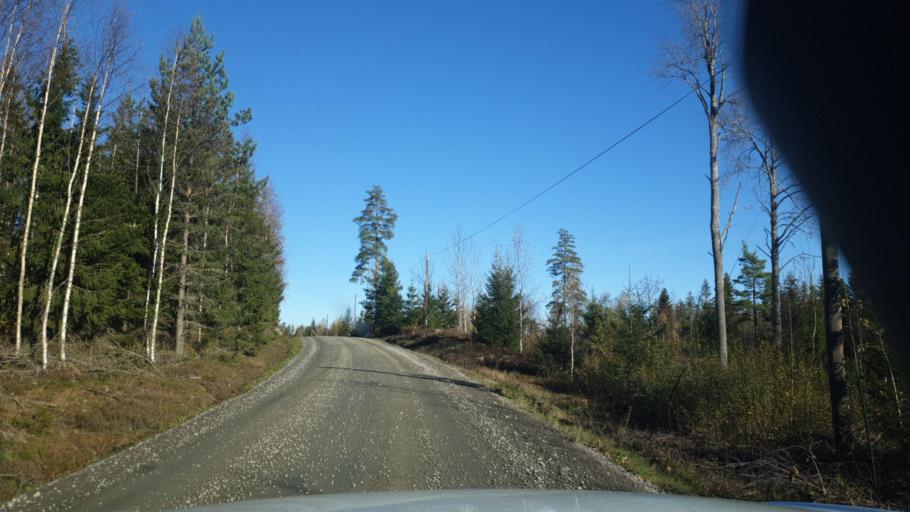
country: SE
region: Vaermland
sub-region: Karlstads Kommun
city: Edsvalla
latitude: 59.5069
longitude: 13.2063
